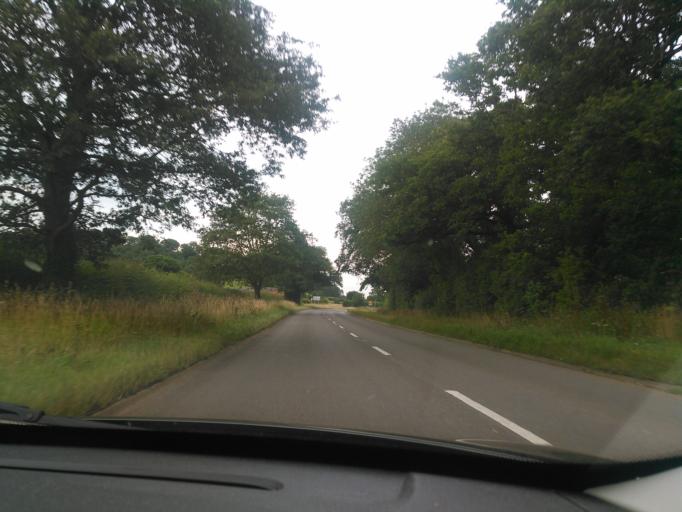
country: GB
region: England
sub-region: Shropshire
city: Stoke upon Tern
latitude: 52.8367
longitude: -2.5953
